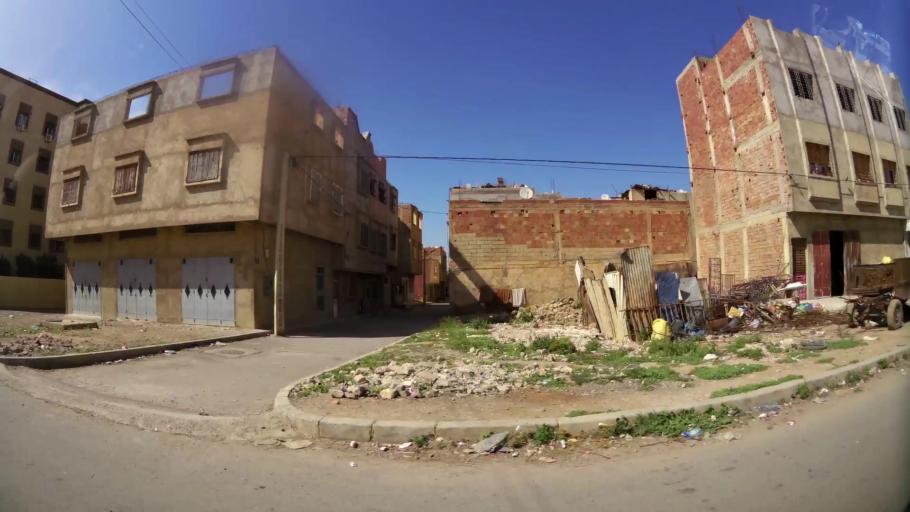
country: MA
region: Oriental
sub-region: Oujda-Angad
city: Oujda
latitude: 34.6987
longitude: -1.8727
